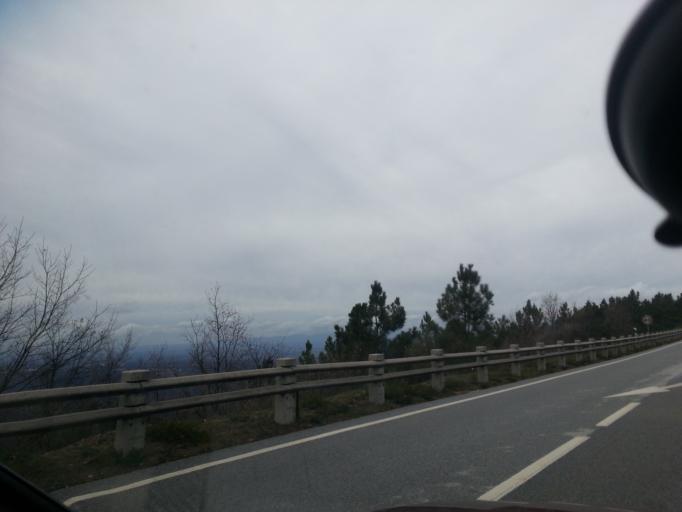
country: PT
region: Guarda
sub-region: Seia
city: Seia
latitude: 40.3462
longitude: -7.7134
